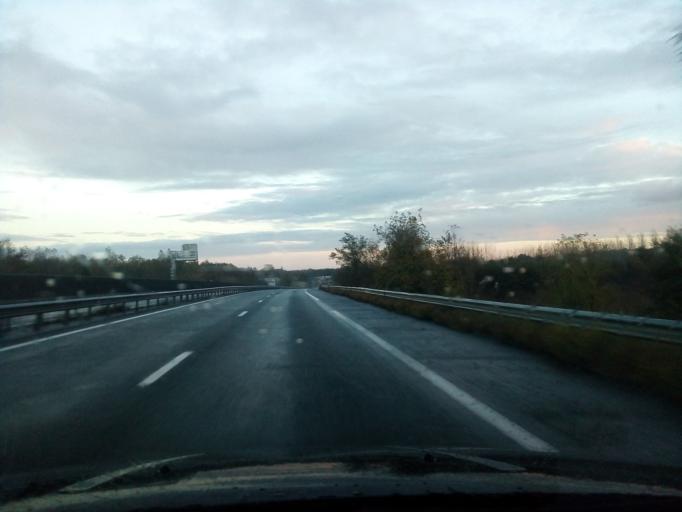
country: FR
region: Aquitaine
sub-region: Departement de la Gironde
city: Cavignac
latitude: 45.1041
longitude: -0.3806
